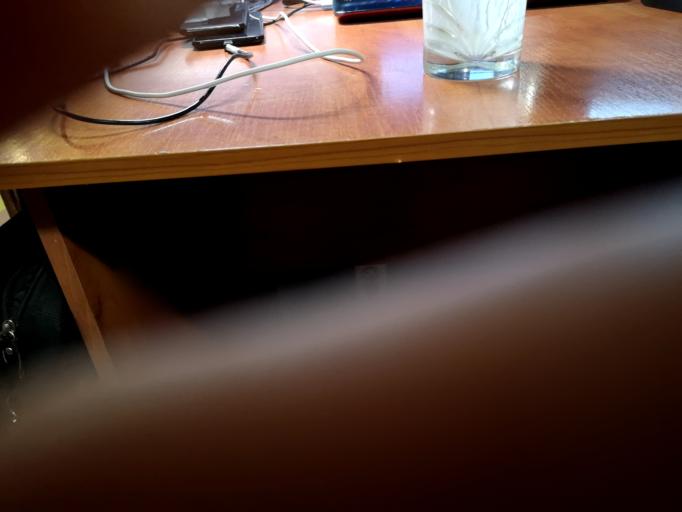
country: RU
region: Sverdlovsk
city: Volchansk
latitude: 59.9004
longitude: 60.2000
